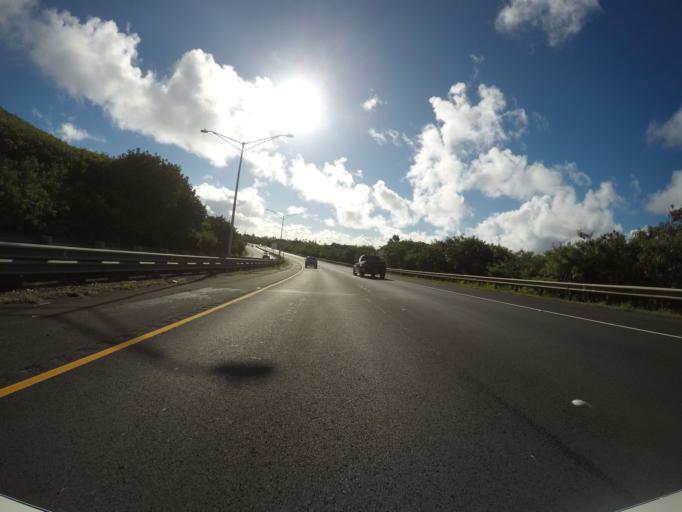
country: US
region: Hawaii
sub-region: Honolulu County
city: Kailua
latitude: 21.4059
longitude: -157.7611
